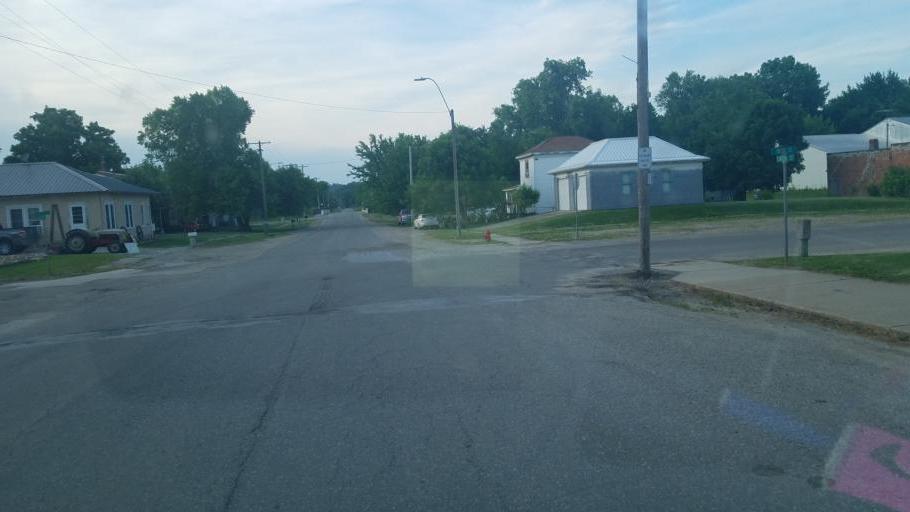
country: US
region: Iowa
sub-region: Benton County
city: Belle Plaine
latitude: 41.9201
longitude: -92.3947
